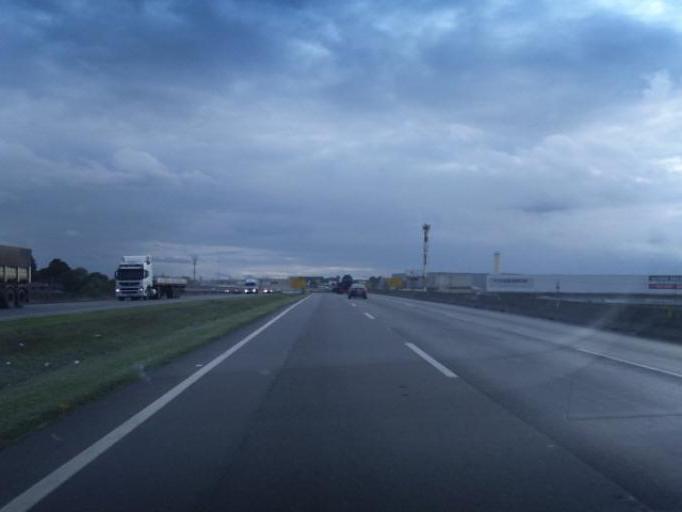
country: BR
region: Parana
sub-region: Sao Jose Dos Pinhais
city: Sao Jose dos Pinhais
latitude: -25.5352
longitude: -49.1478
